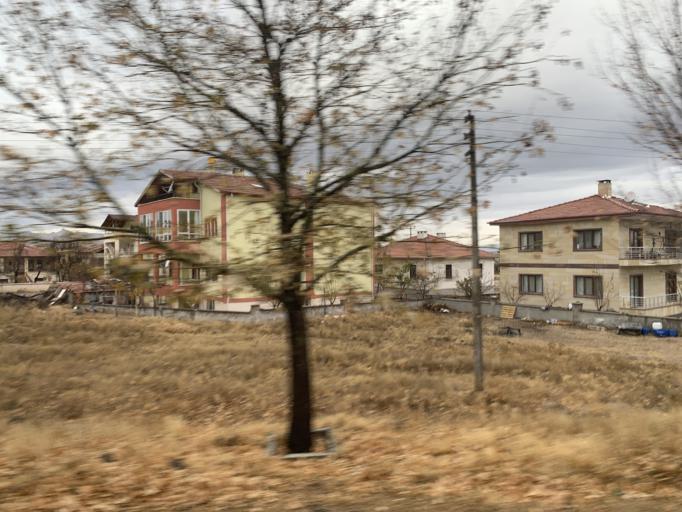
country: TR
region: Nevsehir
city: Avanos
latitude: 38.7075
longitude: 34.8577
